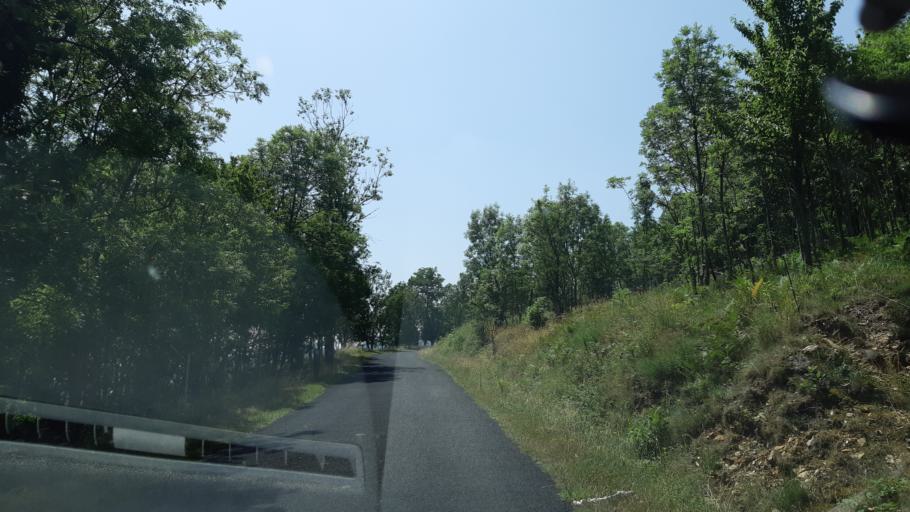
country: FR
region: Languedoc-Roussillon
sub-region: Departement des Pyrenees-Orientales
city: Arles
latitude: 42.5444
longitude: 2.5812
